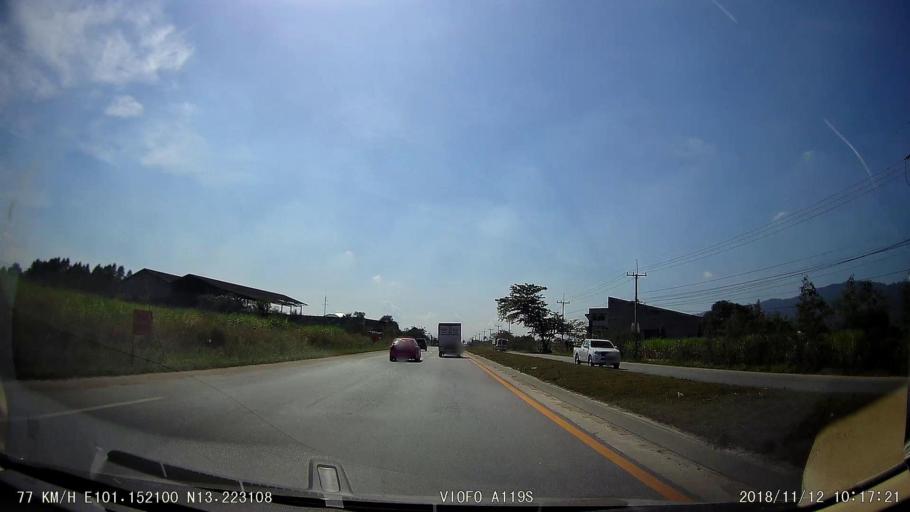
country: TH
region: Chon Buri
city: Ban Bueng
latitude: 13.2227
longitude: 101.1522
